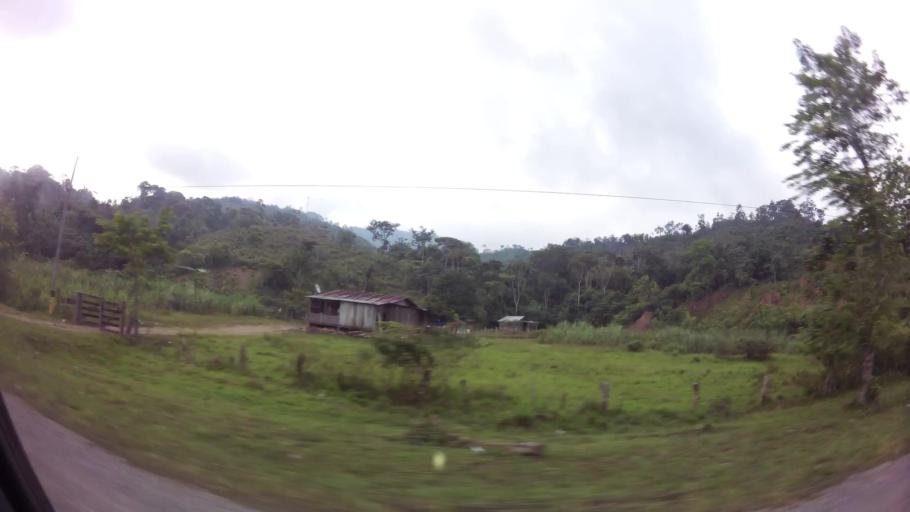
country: HN
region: Yoro
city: Guaimitas
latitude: 15.5058
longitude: -87.6941
